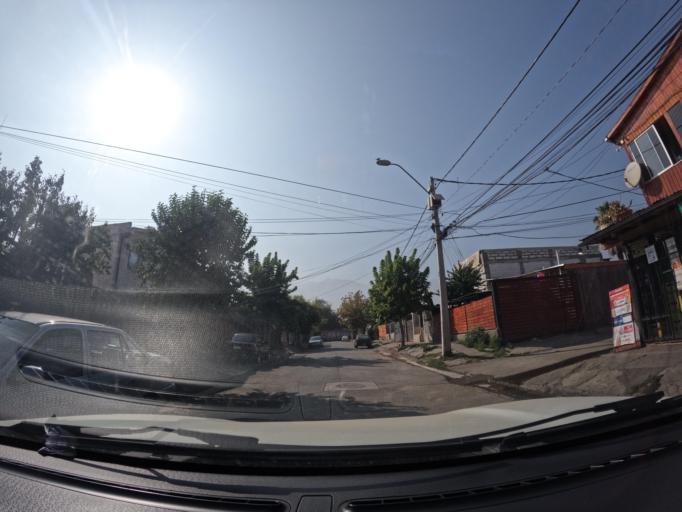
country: CL
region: Santiago Metropolitan
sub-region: Provincia de Santiago
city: Villa Presidente Frei, Nunoa, Santiago, Chile
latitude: -33.4801
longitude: -70.5631
